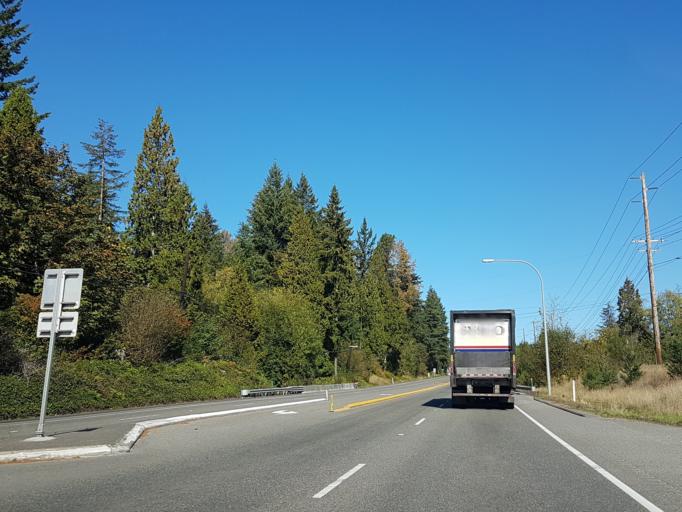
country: US
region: Washington
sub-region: Snohomish County
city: Maltby
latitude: 47.7983
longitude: -122.1433
